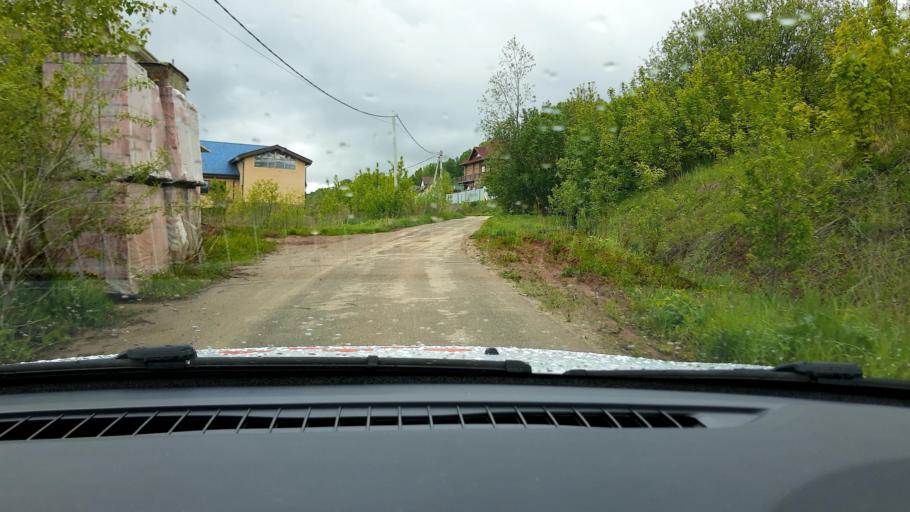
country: RU
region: Nizjnij Novgorod
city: Afonino
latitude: 56.2687
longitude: 44.0988
